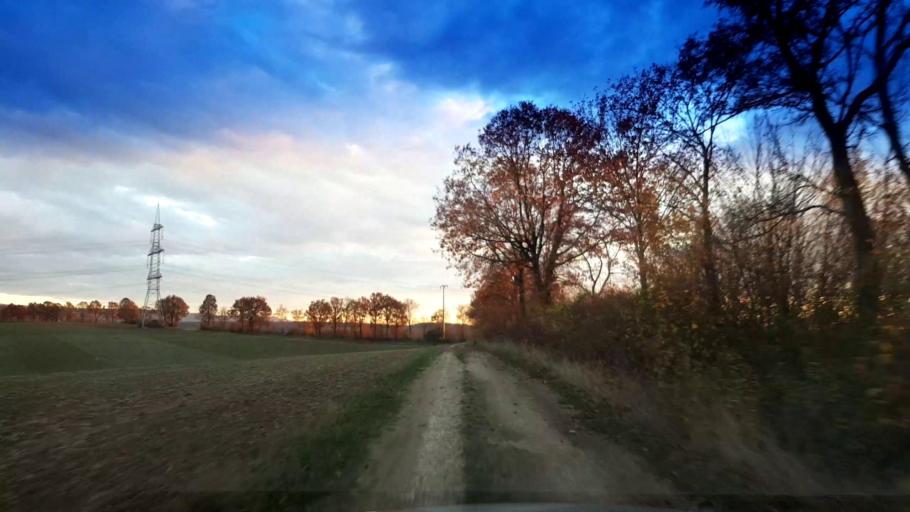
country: DE
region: Bavaria
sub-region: Upper Franconia
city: Memmelsdorf
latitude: 49.9617
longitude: 10.9767
